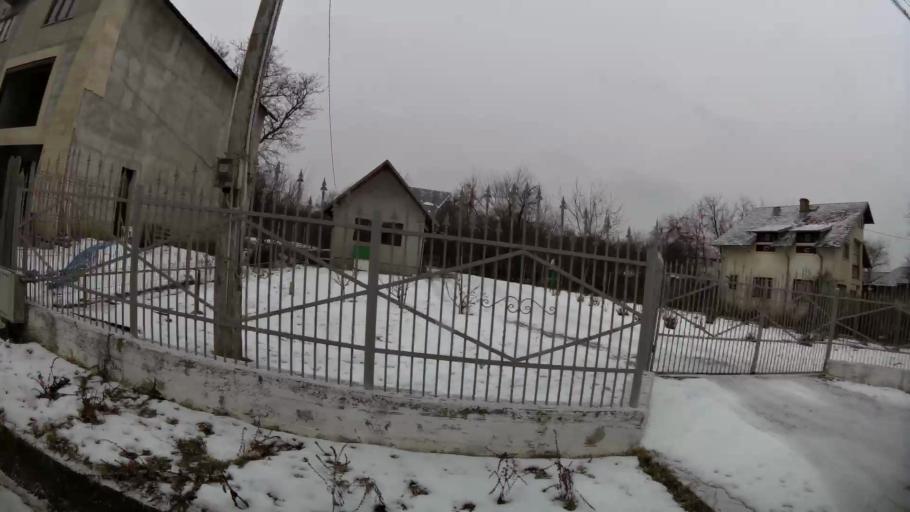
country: RO
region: Dambovita
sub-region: Municipiul Targoviste
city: Targoviste
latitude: 44.9385
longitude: 25.4742
